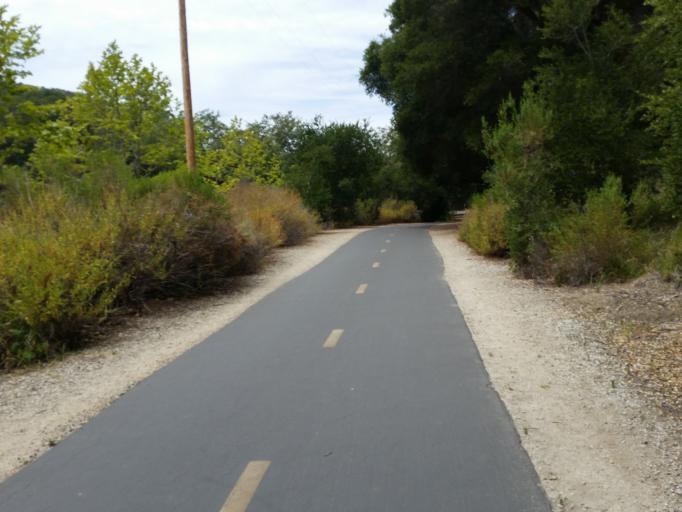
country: US
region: California
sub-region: San Luis Obispo County
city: Avila Beach
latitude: 35.1881
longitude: -120.7119
